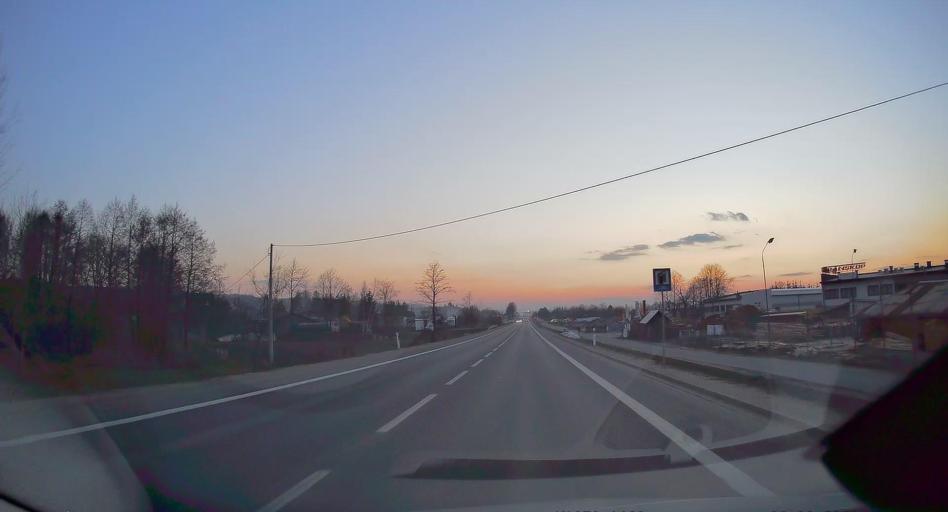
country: PL
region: Subcarpathian Voivodeship
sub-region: Powiat debicki
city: Debica
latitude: 50.0399
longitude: 21.4236
